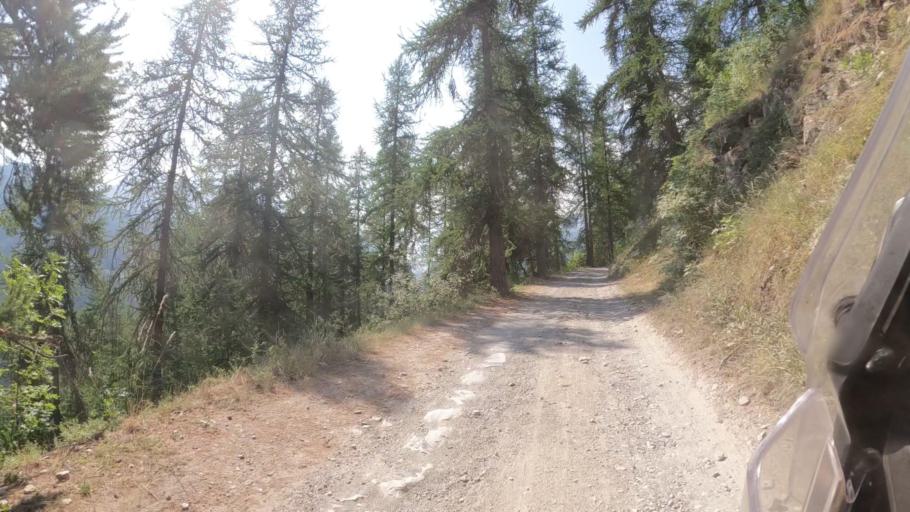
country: IT
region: Piedmont
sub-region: Provincia di Torino
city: Cesana Torinese
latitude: 44.9279
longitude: 6.8135
